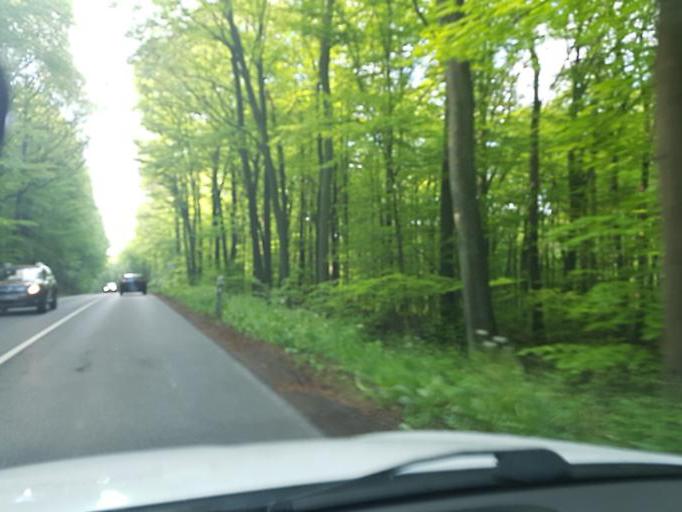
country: DE
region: Hesse
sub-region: Regierungsbezirk Darmstadt
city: Niedernhausen
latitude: 50.1759
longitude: 8.2994
